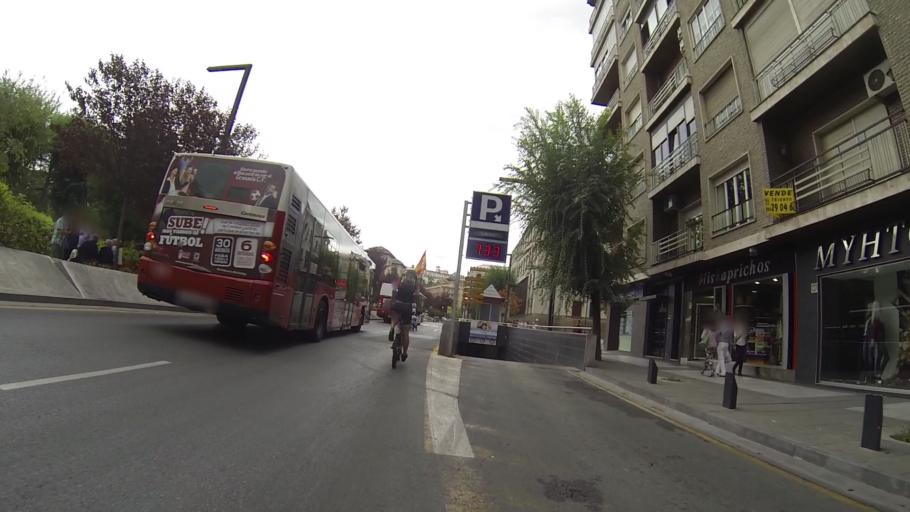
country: ES
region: Andalusia
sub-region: Provincia de Granada
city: Granada
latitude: 37.1835
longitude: -3.6033
